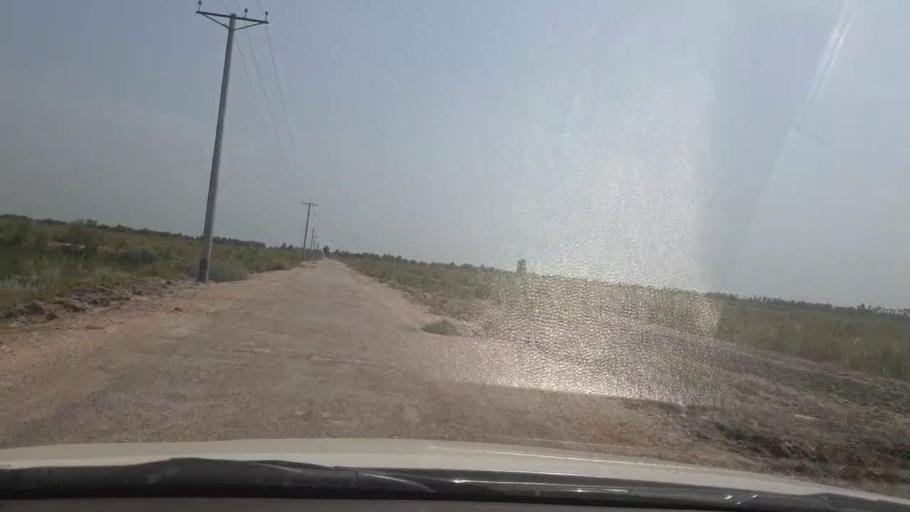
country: PK
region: Sindh
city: Garhi Yasin
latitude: 27.9836
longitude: 68.5023
